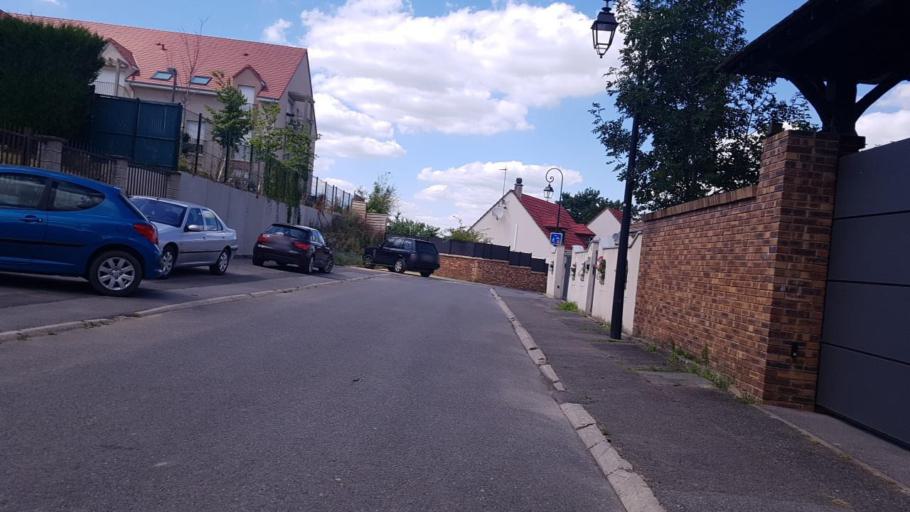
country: FR
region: Ile-de-France
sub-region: Departement de Seine-et-Marne
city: Moussy-le-Vieux
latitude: 49.0496
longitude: 2.6234
